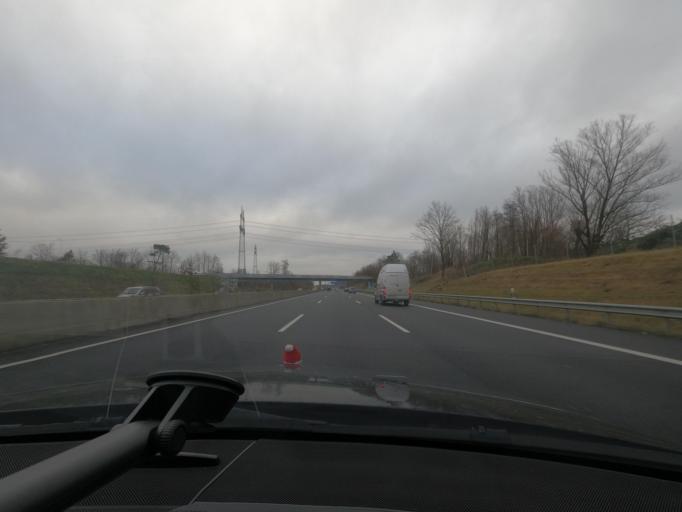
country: DE
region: Schleswig-Holstein
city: Ellerau
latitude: 53.7369
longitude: 9.9448
